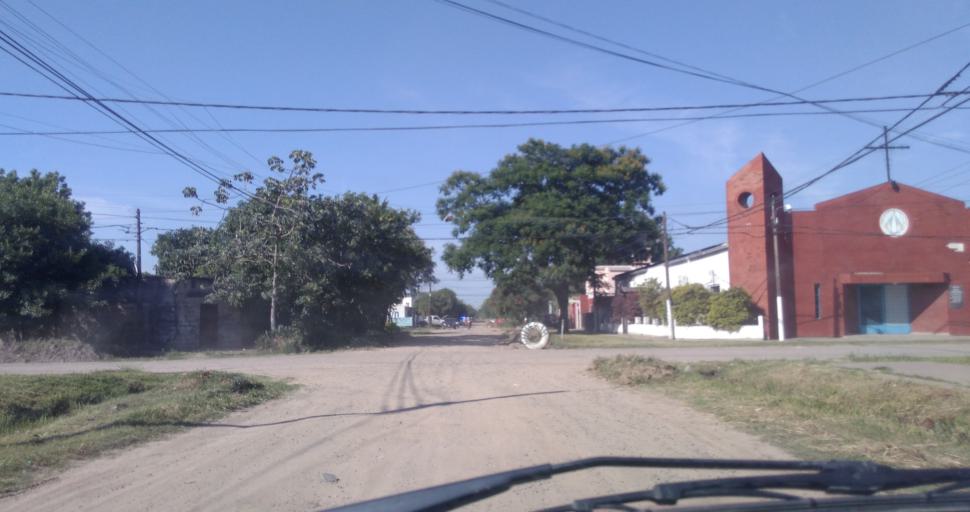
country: AR
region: Chaco
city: Resistencia
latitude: -27.4678
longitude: -58.9708
